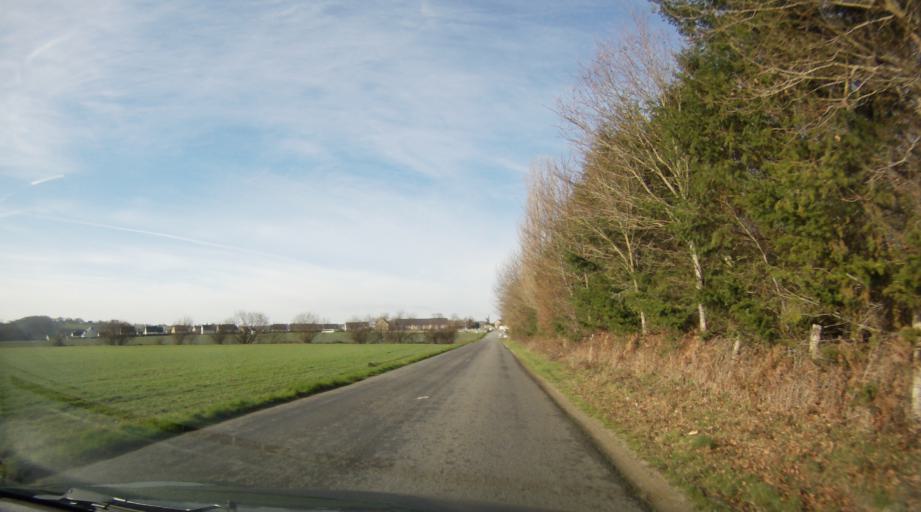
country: FR
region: Brittany
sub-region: Departement d'Ille-et-Vilaine
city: Orgeres
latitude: 47.9950
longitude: -1.6605
